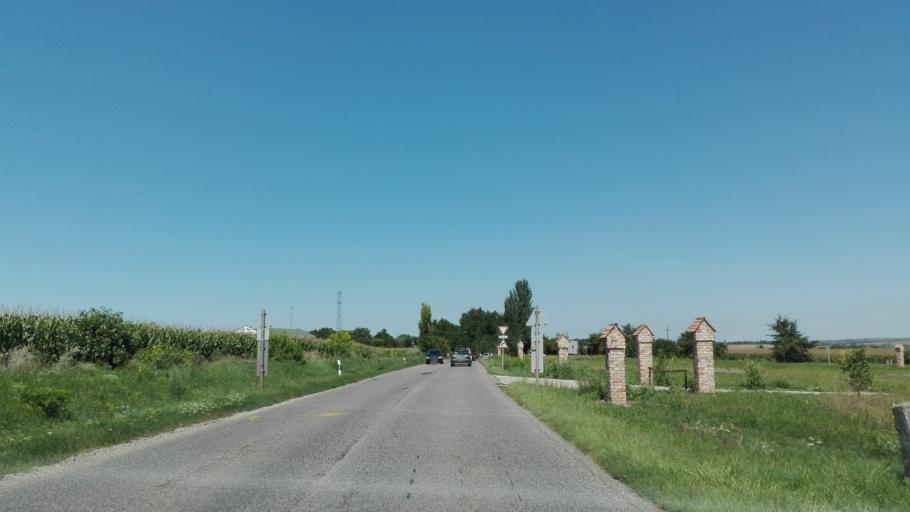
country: HU
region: Fejer
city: Lepseny
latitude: 46.9865
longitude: 18.1916
